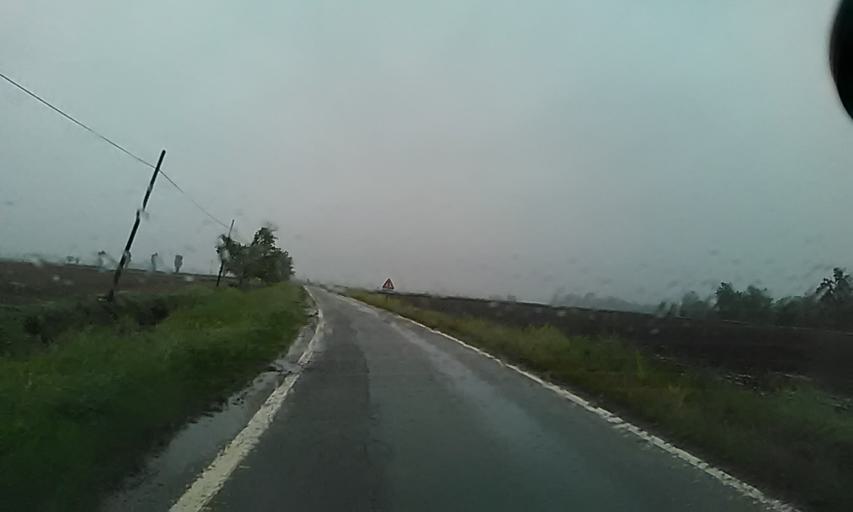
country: IT
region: Piedmont
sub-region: Provincia di Vercelli
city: San Giacomo Vercellese
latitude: 45.4832
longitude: 8.3371
